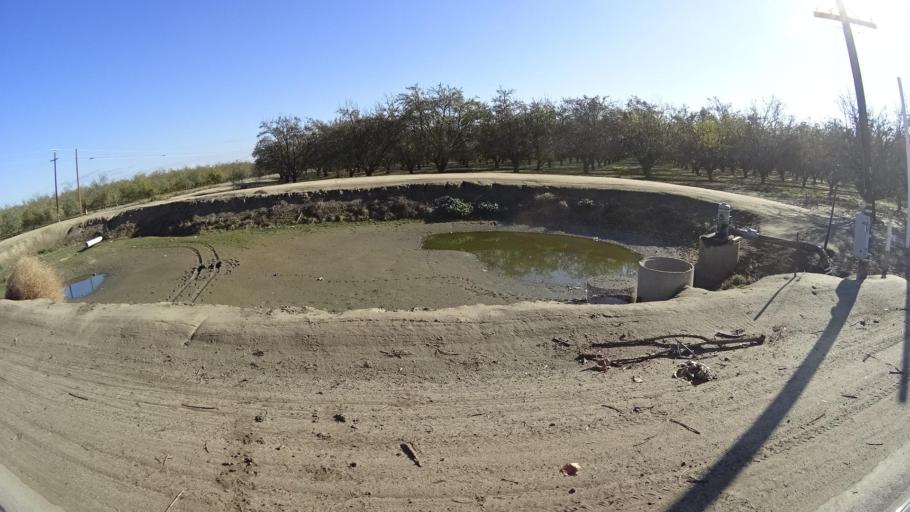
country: US
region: California
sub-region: Kern County
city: McFarland
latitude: 35.6884
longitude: -119.2677
